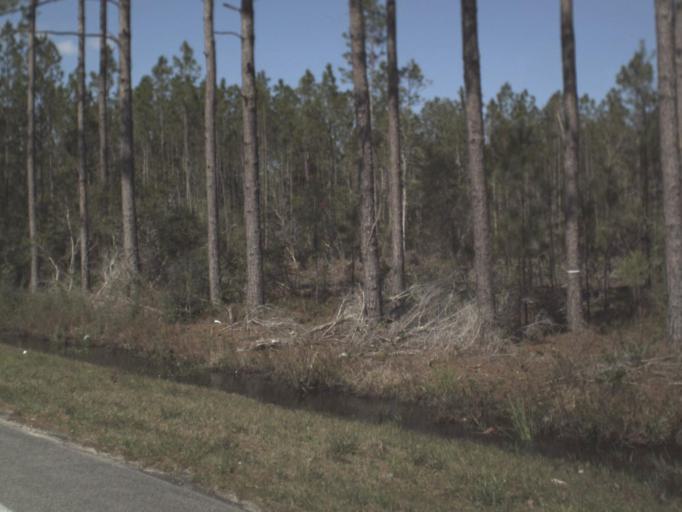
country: US
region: Florida
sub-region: Gulf County
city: Wewahitchka
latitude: 29.9817
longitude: -85.1669
